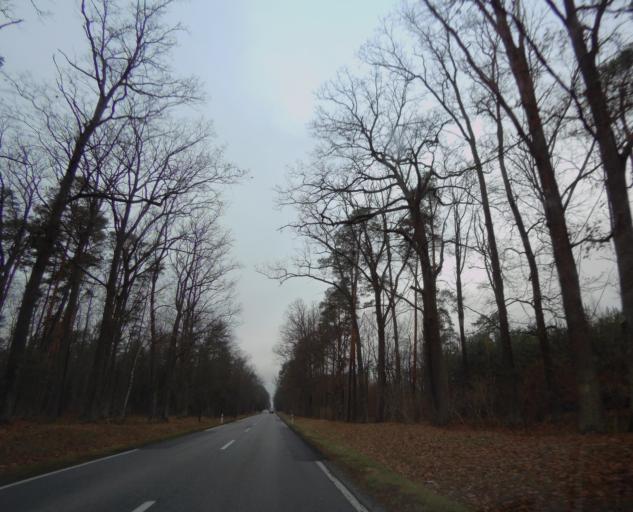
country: PL
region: Subcarpathian Voivodeship
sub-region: Powiat nizanski
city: Krzeszow
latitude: 50.3901
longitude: 22.3038
